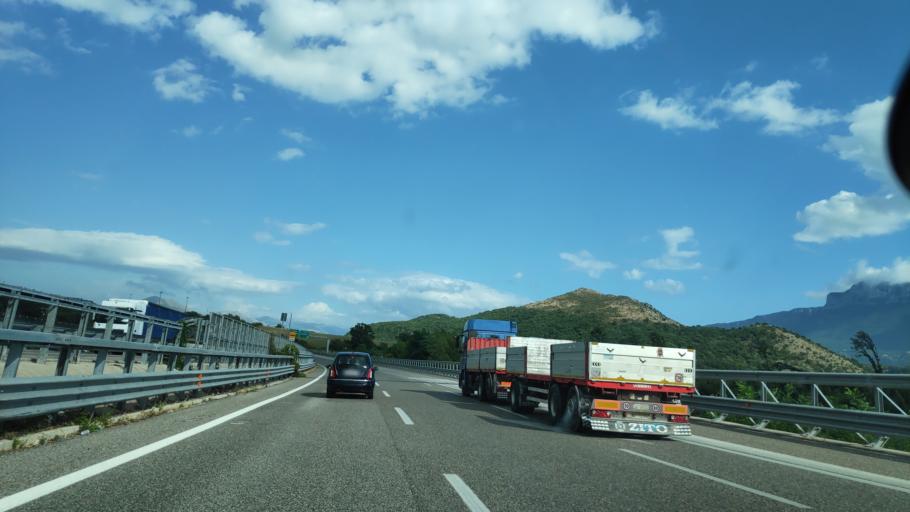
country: IT
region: Campania
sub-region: Provincia di Salerno
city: Palomonte
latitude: 40.6112
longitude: 15.2845
